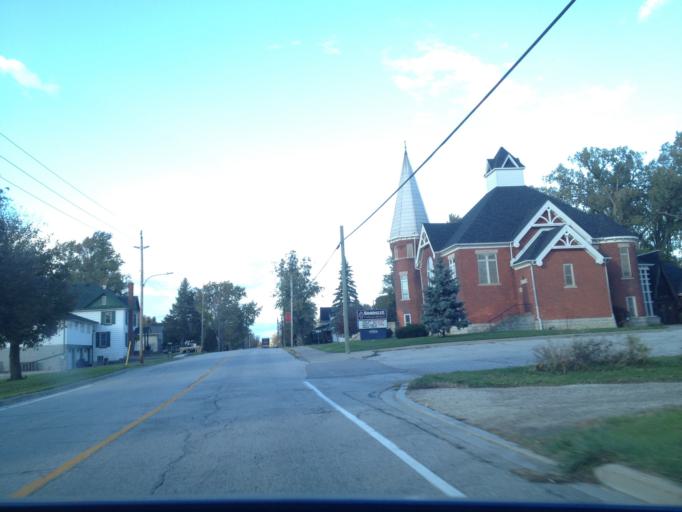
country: US
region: Michigan
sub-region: Wayne County
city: Grosse Pointe
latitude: 42.1963
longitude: -82.7191
